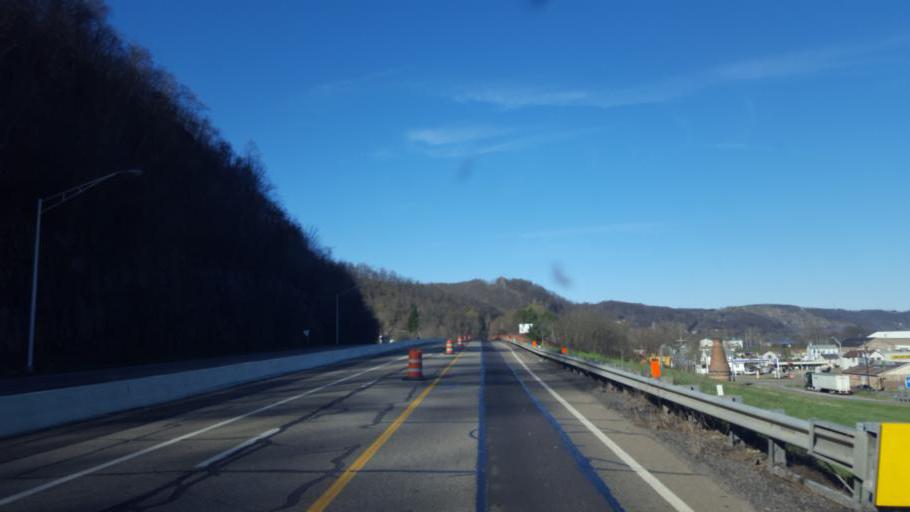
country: US
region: Ohio
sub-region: Columbiana County
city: Wellsville
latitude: 40.6110
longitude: -80.6452
